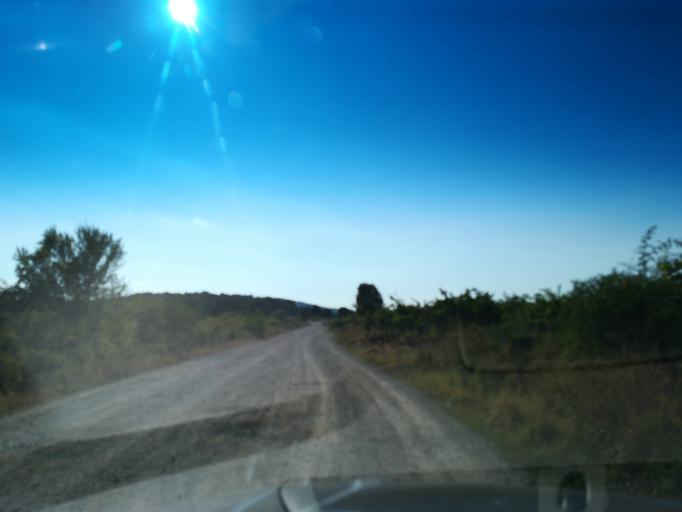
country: BG
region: Khaskovo
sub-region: Obshtina Mineralni Bani
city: Mineralni Bani
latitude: 41.9716
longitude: 25.3415
